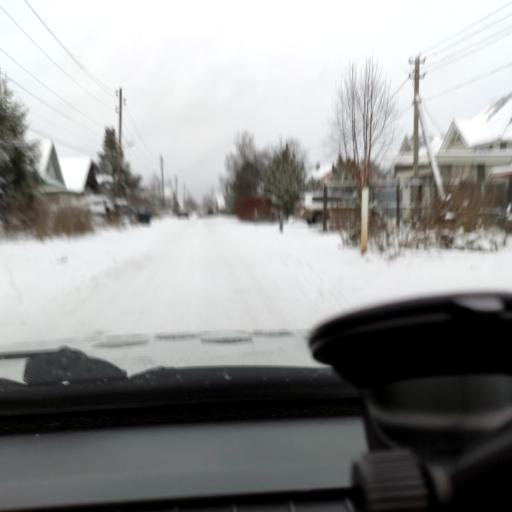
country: RU
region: Perm
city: Perm
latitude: 58.0519
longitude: 56.3573
